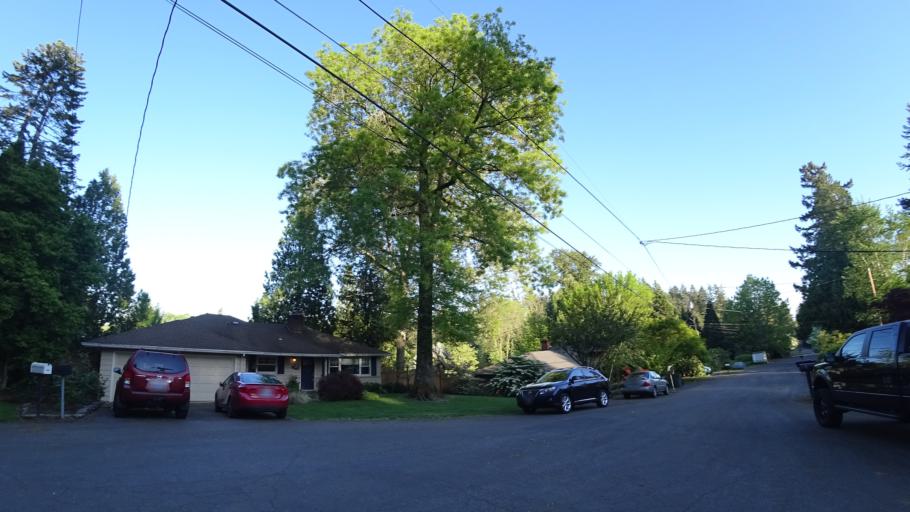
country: US
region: Oregon
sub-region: Washington County
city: West Slope
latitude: 45.4930
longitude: -122.7737
